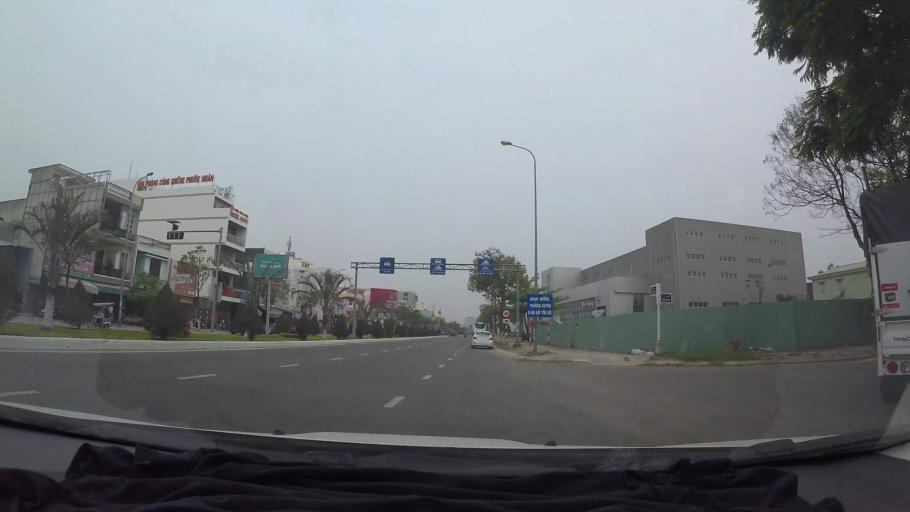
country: VN
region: Da Nang
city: Cam Le
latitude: 16.0209
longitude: 108.2109
